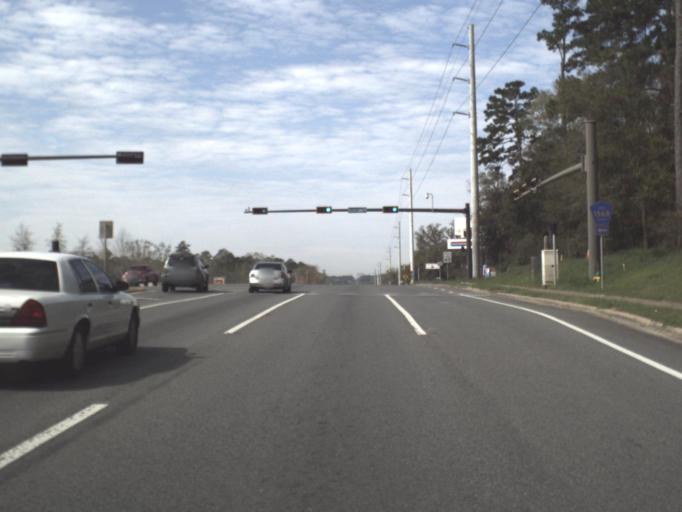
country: US
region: Florida
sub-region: Leon County
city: Tallahassee
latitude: 30.4651
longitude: -84.2143
